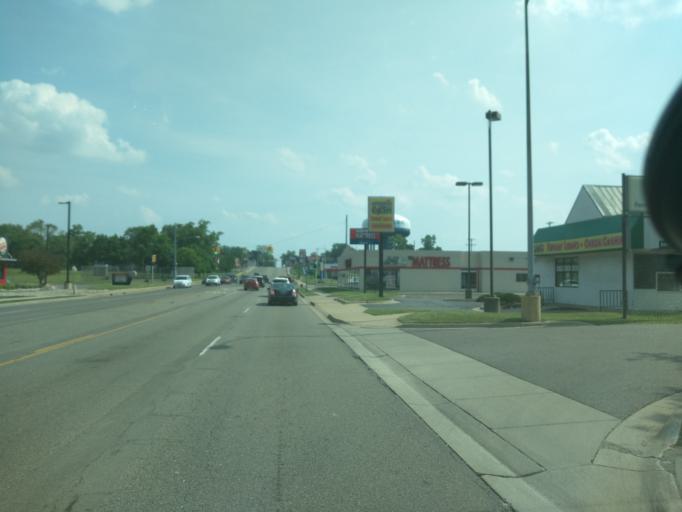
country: US
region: Michigan
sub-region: Jackson County
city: Jackson
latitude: 42.2628
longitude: -84.4235
